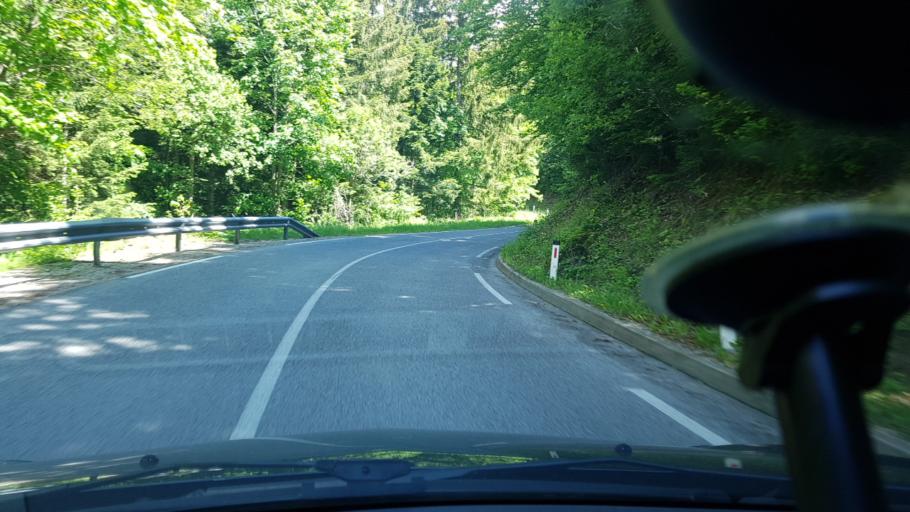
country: SI
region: Zrece
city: Zrece
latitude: 46.4294
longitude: 15.3710
